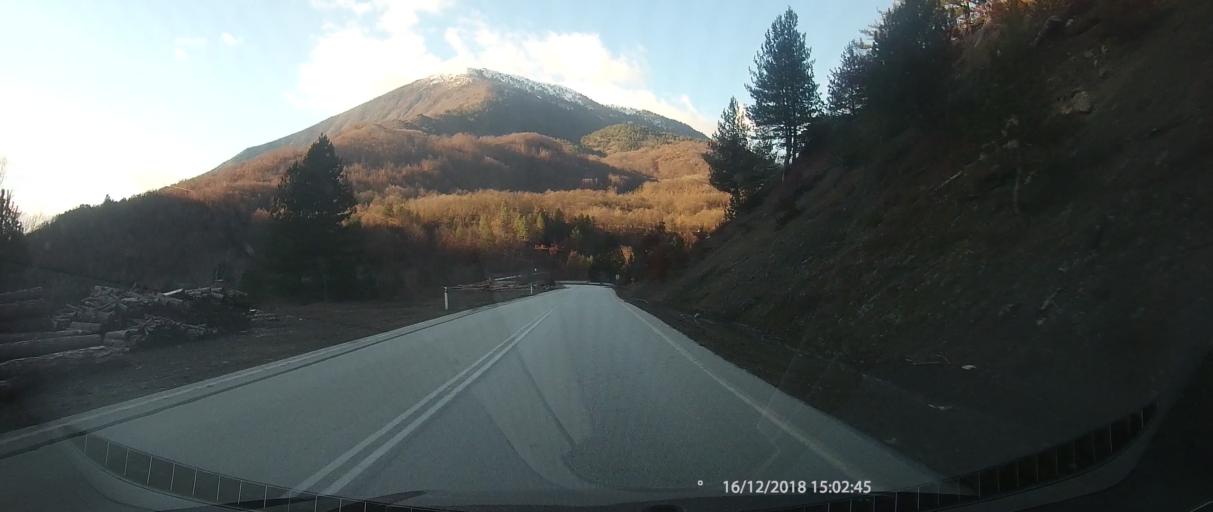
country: GR
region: West Macedonia
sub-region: Nomos Kastorias
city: Nestorio
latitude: 40.2298
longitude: 20.9912
